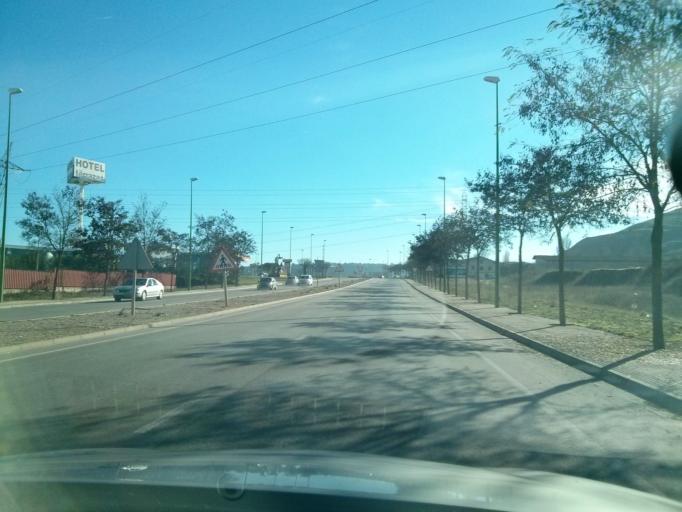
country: ES
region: Castille and Leon
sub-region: Provincia de Burgos
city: Burgos
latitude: 42.3654
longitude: -3.7137
